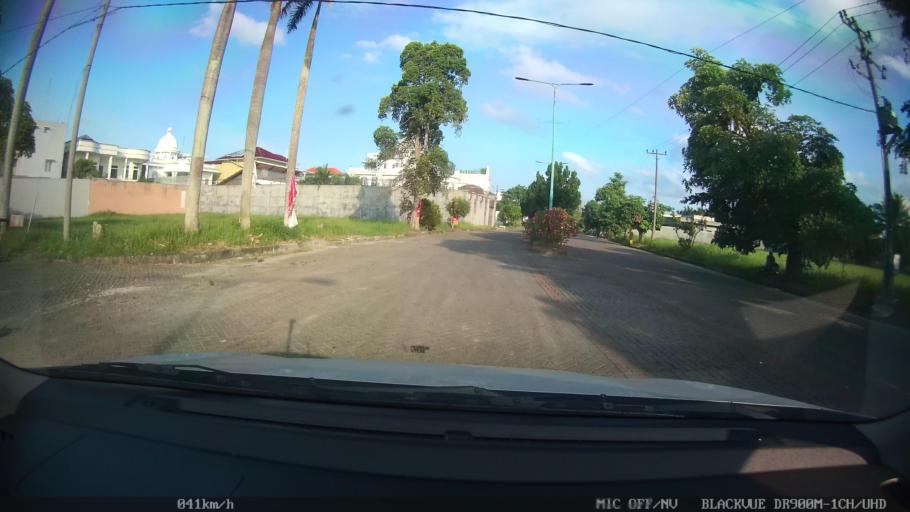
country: ID
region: North Sumatra
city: Medan
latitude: 3.6252
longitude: 98.6516
